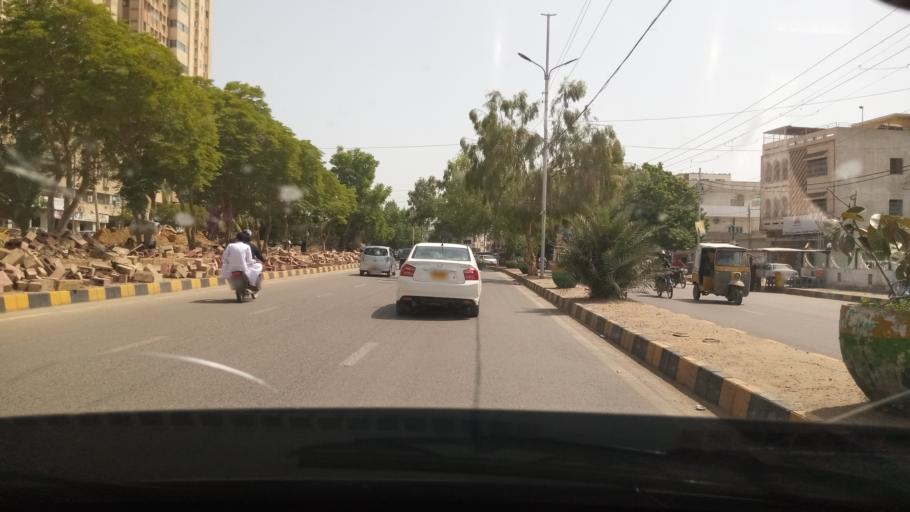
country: PK
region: Sindh
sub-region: Karachi District
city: Karachi
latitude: 24.8720
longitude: 67.0483
